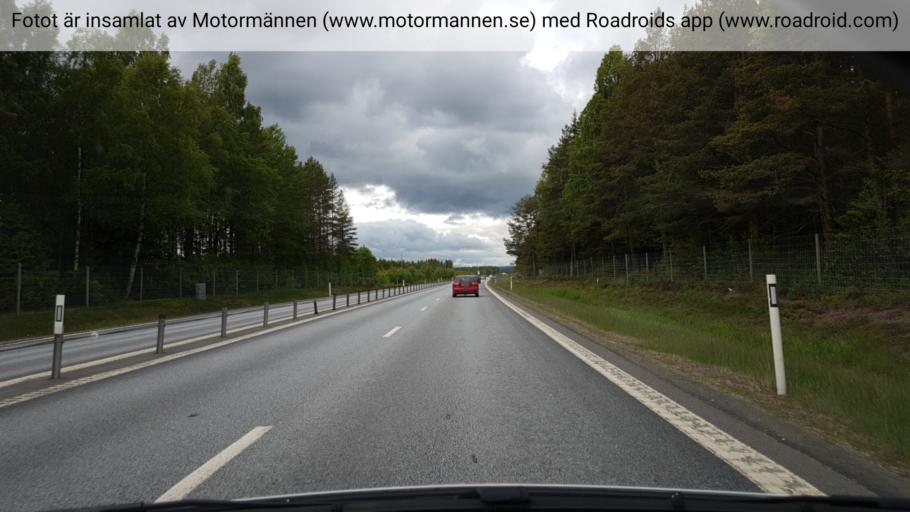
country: SE
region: Vaesterbotten
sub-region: Nordmalings Kommun
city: Nordmaling
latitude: 63.5842
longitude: 19.5936
